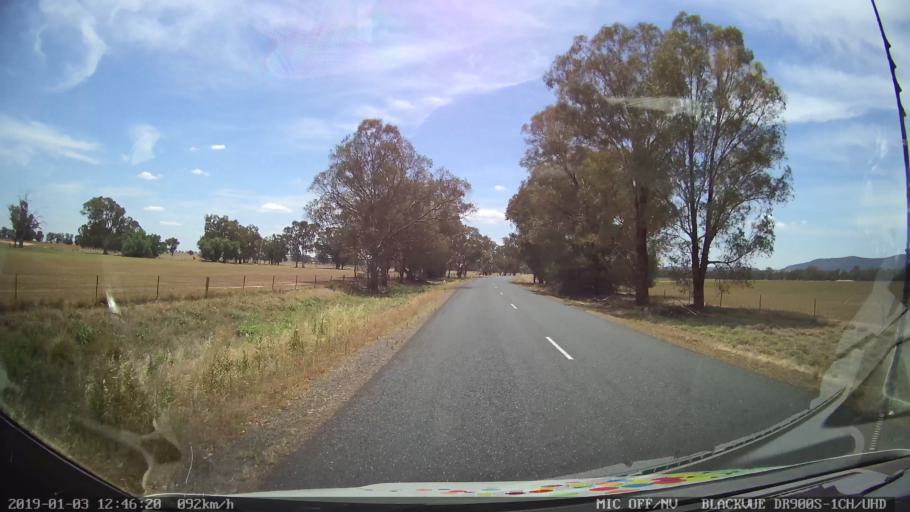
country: AU
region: New South Wales
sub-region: Weddin
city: Grenfell
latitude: -33.7393
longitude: 148.2321
